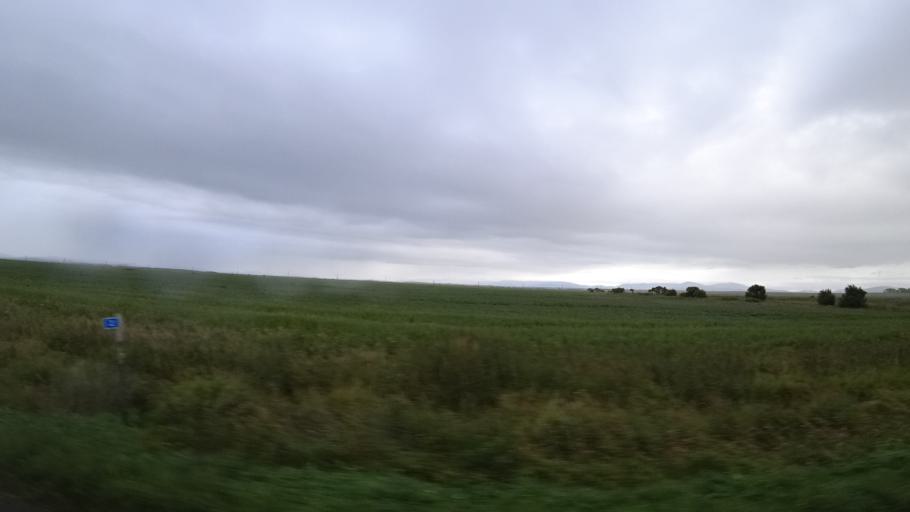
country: RU
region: Primorskiy
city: Chernigovka
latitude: 44.3827
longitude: 132.5296
